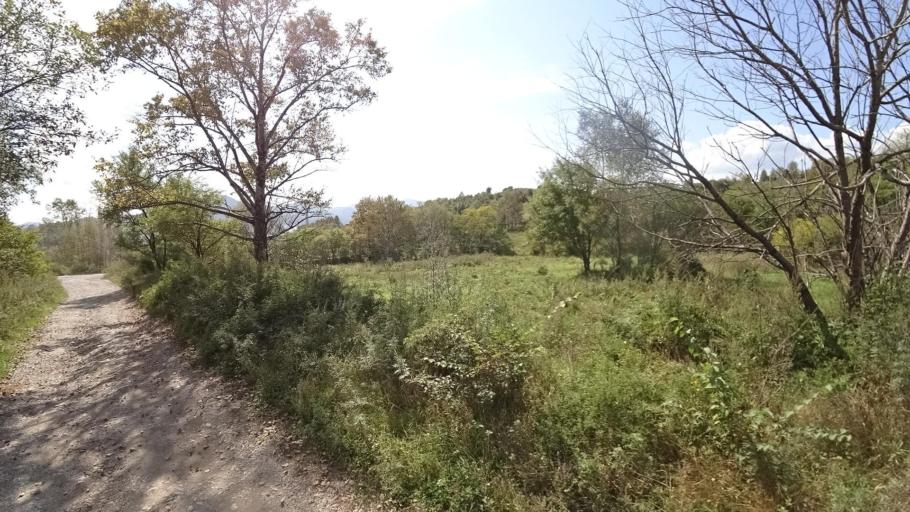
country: RU
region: Jewish Autonomous Oblast
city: Londoko
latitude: 49.0115
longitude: 131.8970
